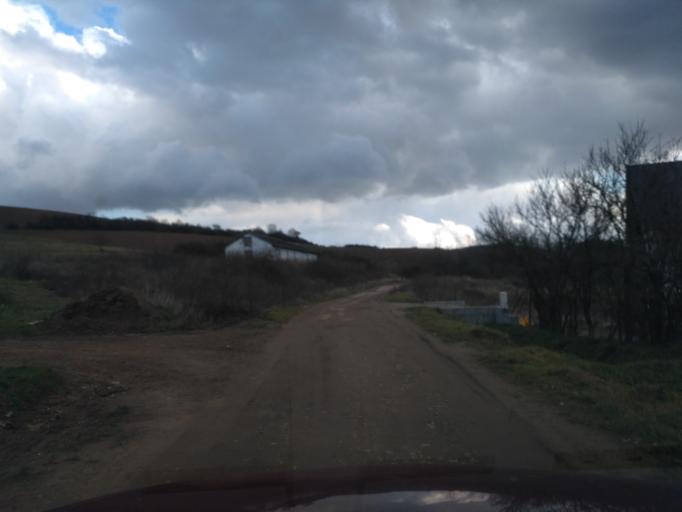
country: SK
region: Presovsky
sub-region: Okres Presov
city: Presov
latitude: 48.9307
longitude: 21.1932
